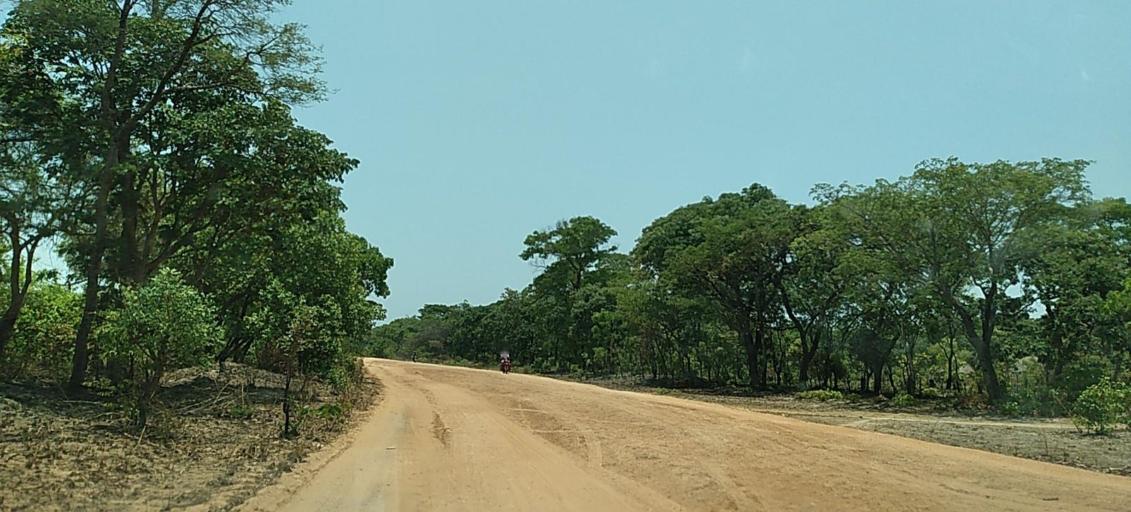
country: ZM
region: Copperbelt
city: Mpongwe
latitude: -13.8071
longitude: 27.8561
